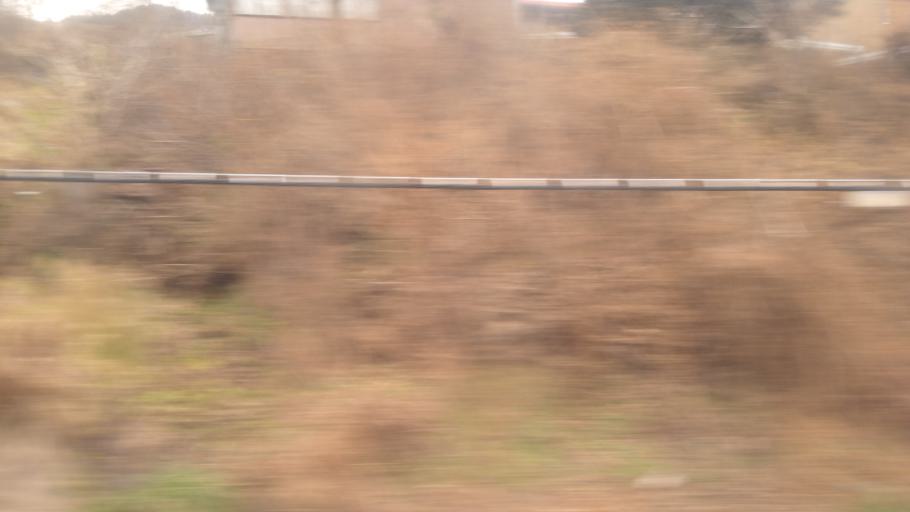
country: JP
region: Nagano
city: Ina
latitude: 35.9408
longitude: 137.7844
